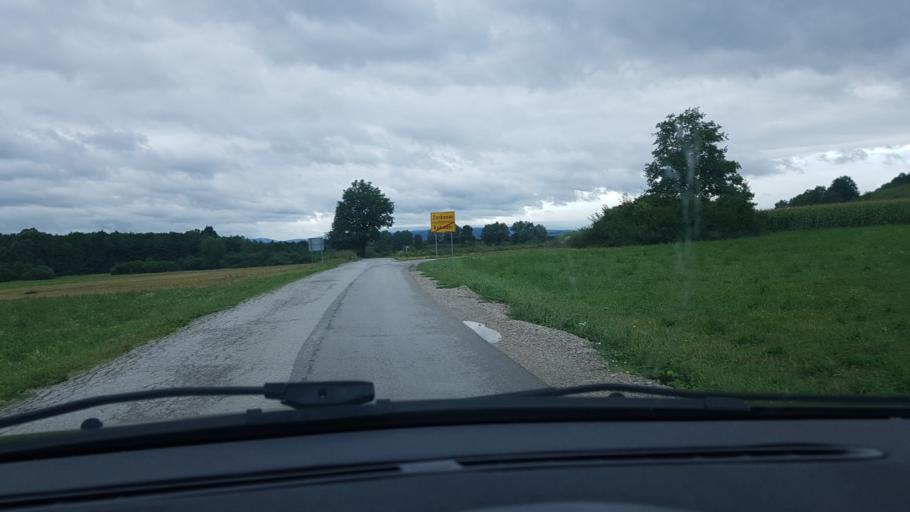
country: HR
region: Karlovacka
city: Ozalj
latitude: 45.5818
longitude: 15.5397
